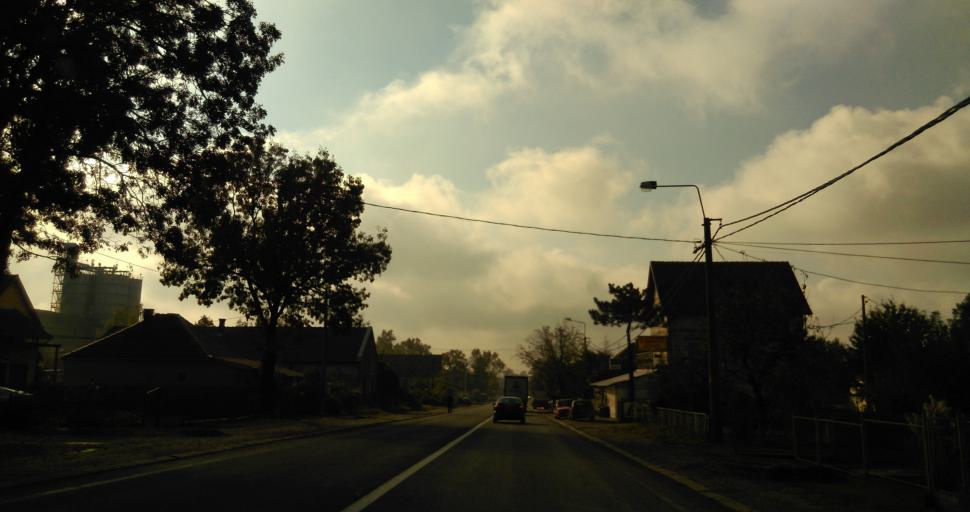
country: RS
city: Stepojevac
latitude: 44.5167
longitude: 20.2934
